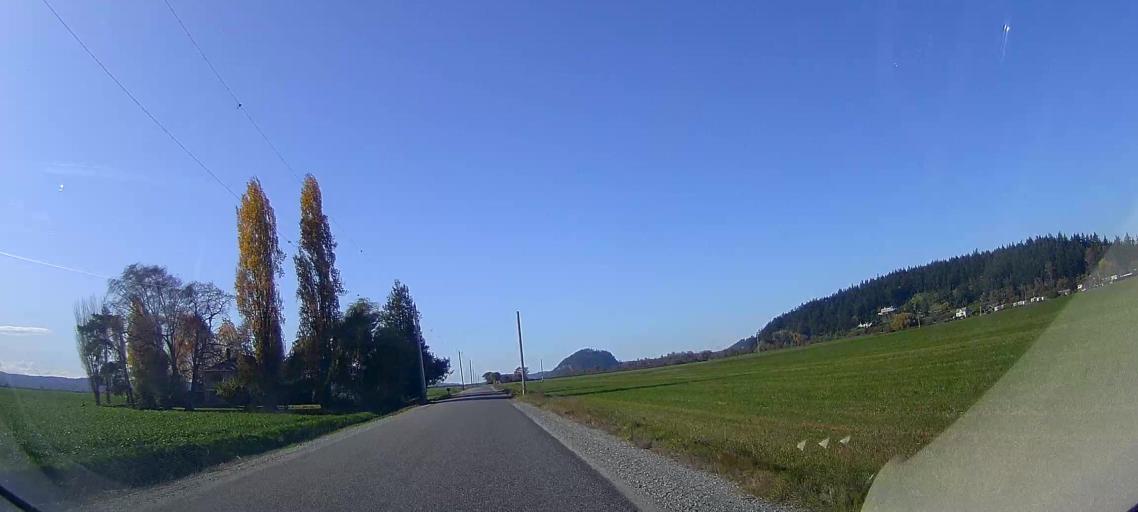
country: US
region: Washington
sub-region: Skagit County
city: Mount Vernon
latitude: 48.3563
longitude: -122.4444
